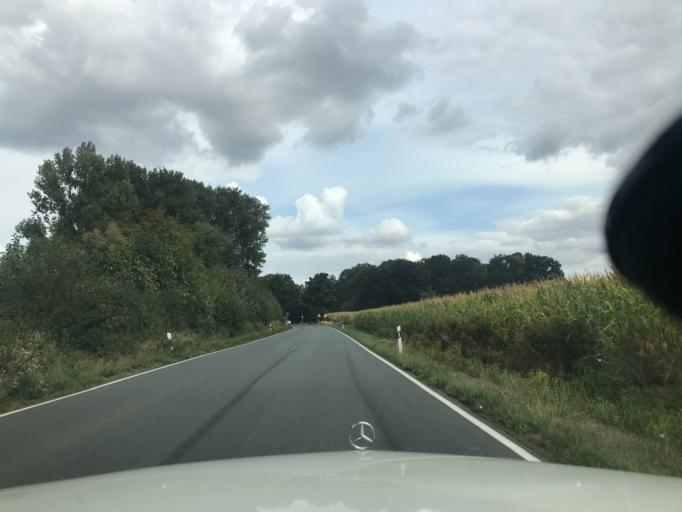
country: DE
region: North Rhine-Westphalia
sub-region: Regierungsbezirk Arnsberg
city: Lippstadt
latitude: 51.6536
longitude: 8.2960
